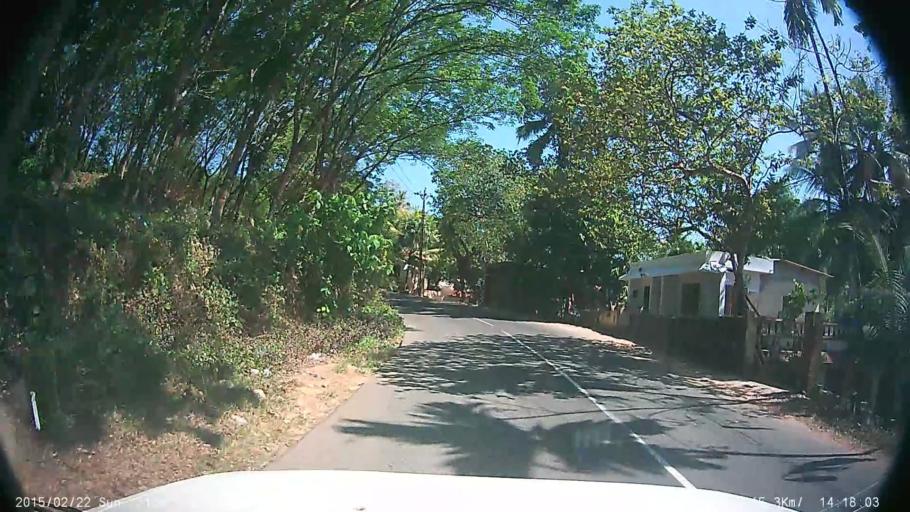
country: IN
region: Kerala
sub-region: Kottayam
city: Lalam
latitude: 9.5637
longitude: 76.6856
